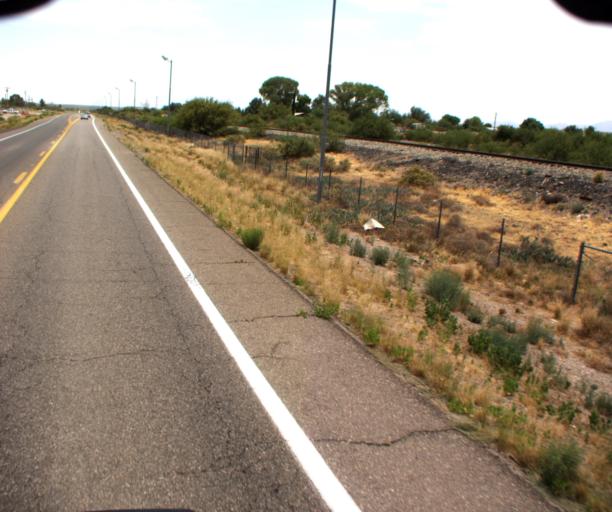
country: US
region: Arizona
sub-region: Graham County
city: Bylas
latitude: 33.1282
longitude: -110.1170
